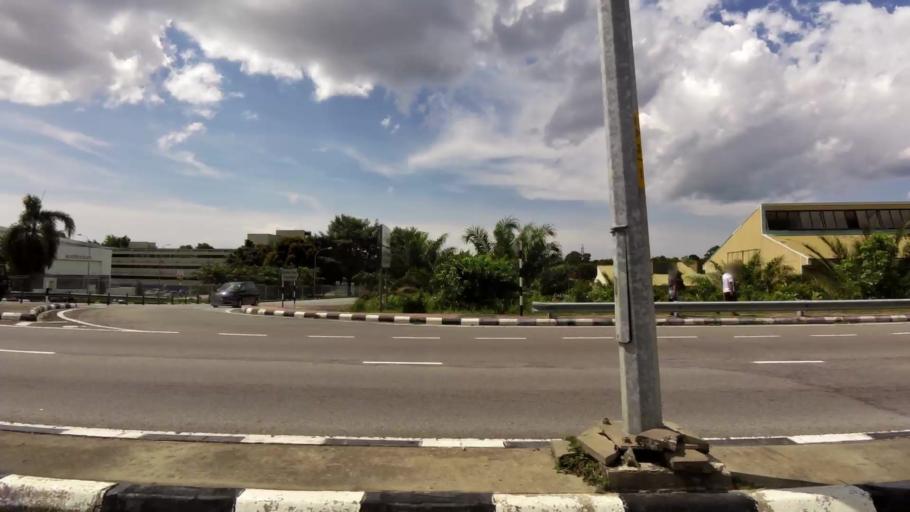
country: BN
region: Brunei and Muara
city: Bandar Seri Begawan
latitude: 4.9455
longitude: 114.9515
